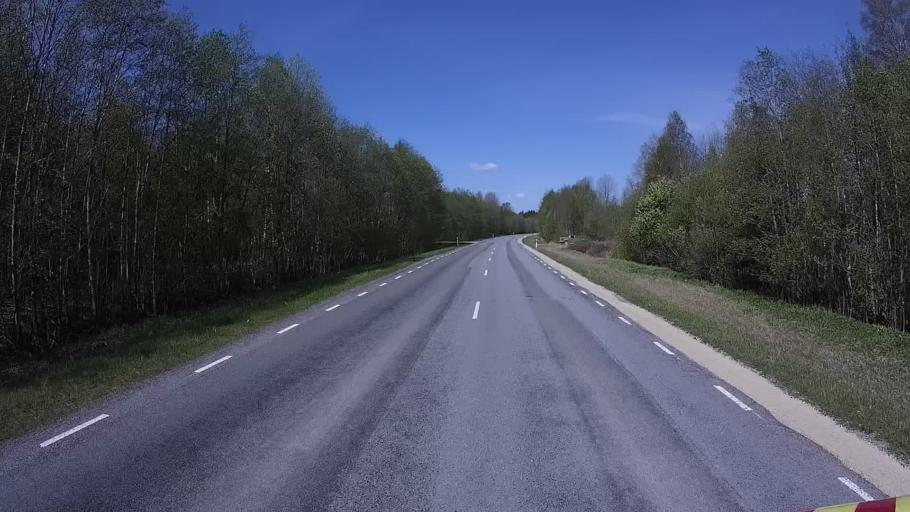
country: EE
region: Laeaene
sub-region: Ridala Parish
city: Uuemoisa
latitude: 58.8402
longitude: 23.6535
